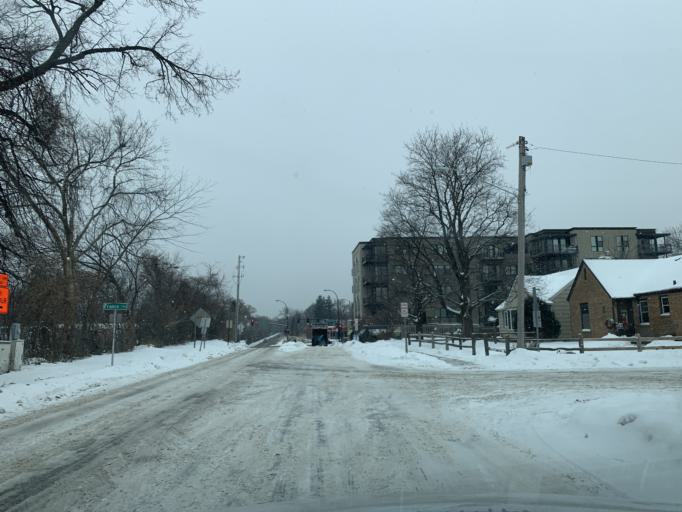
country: US
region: Minnesota
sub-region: Hennepin County
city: Saint Louis Park
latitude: 44.9415
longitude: -93.3291
